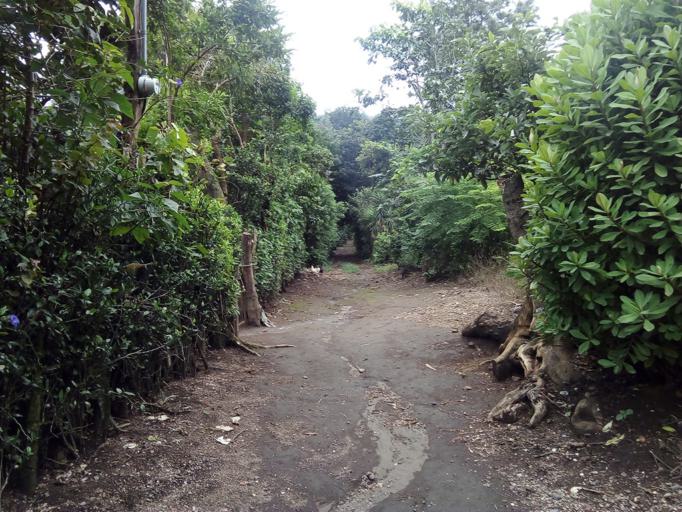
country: GT
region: Escuintla
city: San Vicente Pacaya
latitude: 14.3340
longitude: -90.6094
